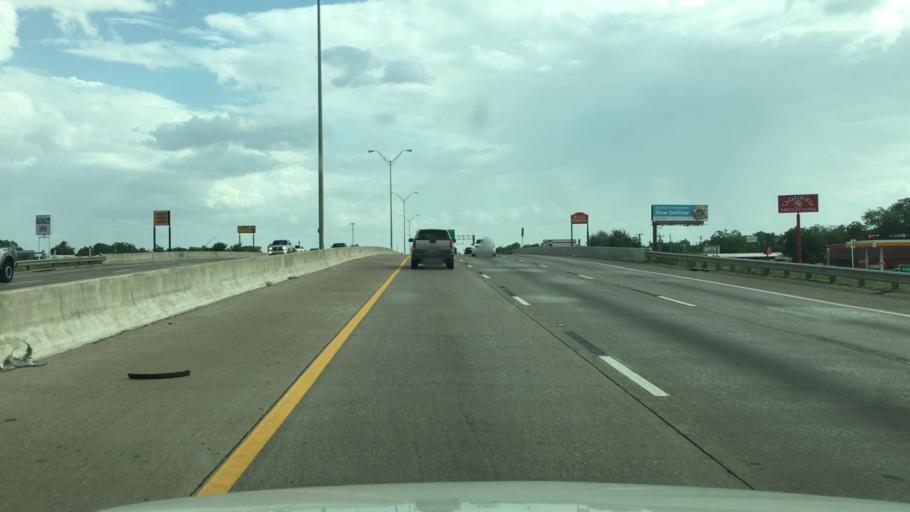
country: US
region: Texas
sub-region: McLennan County
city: Beverly
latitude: 31.5368
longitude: -97.1293
